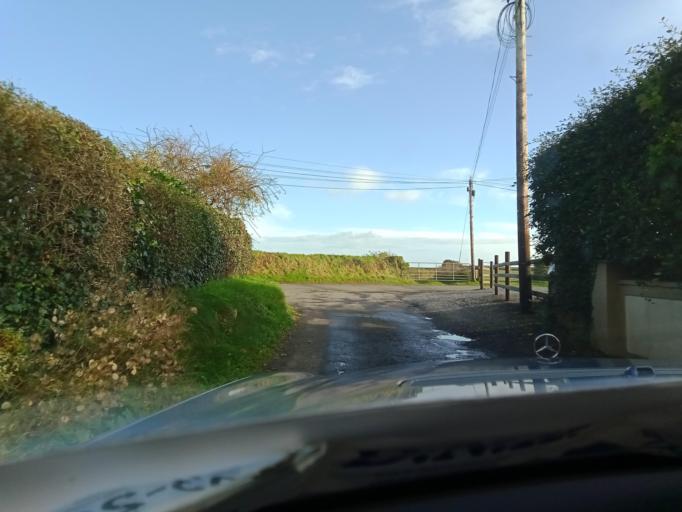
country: IE
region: Leinster
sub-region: Kilkenny
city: Mooncoin
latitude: 52.2801
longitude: -7.2525
